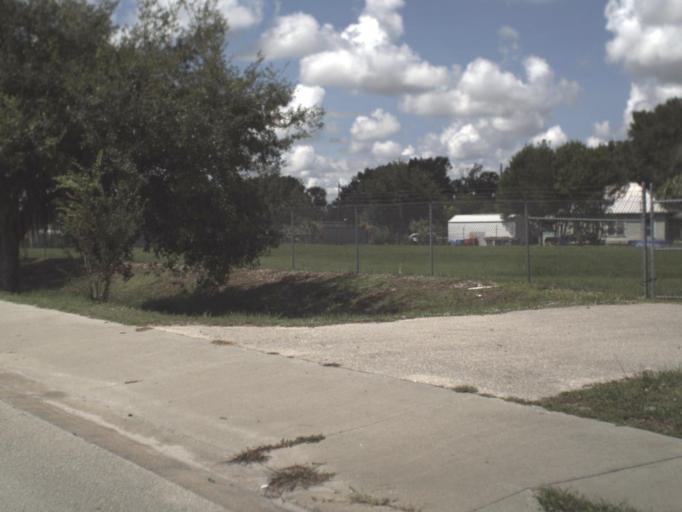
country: US
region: Florida
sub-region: DeSoto County
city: Arcadia
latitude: 27.2212
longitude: -81.8577
